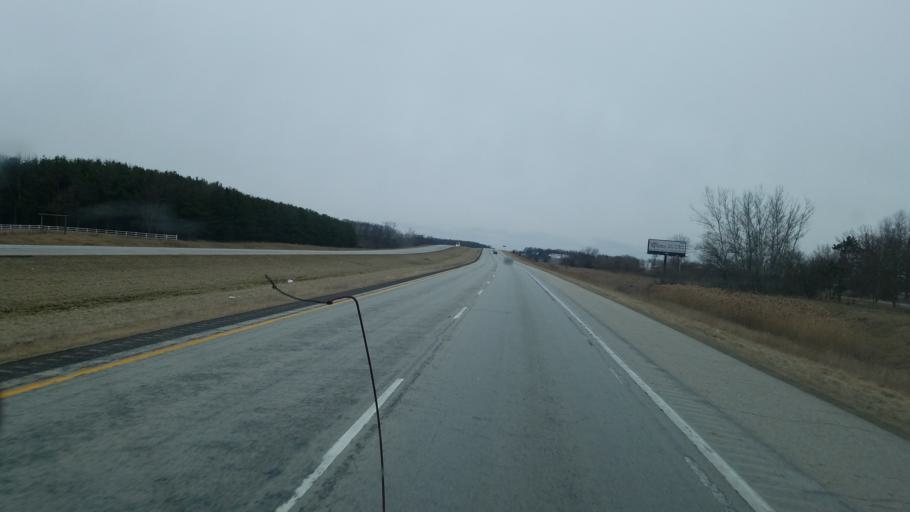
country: US
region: Indiana
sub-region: Fulton County
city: Rochester
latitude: 41.0844
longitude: -86.2412
